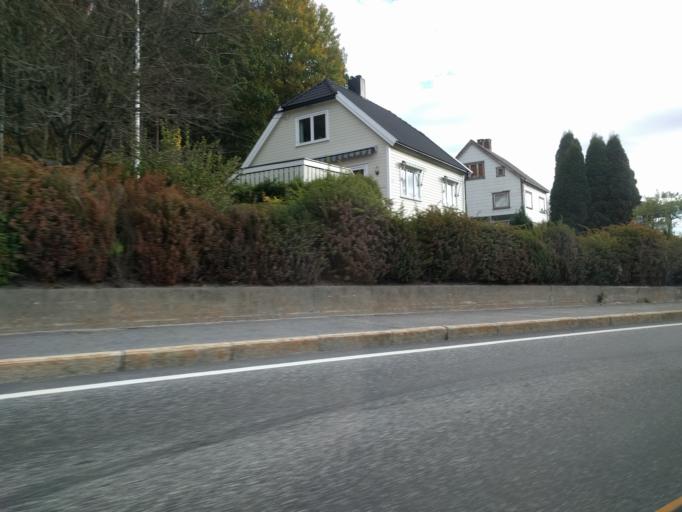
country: NO
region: Vest-Agder
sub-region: Vennesla
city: Vennesla
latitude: 58.2965
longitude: 7.8358
